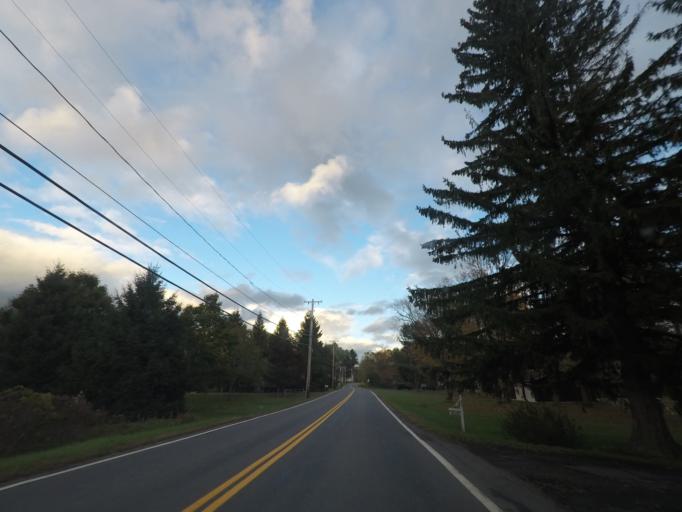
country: US
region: New York
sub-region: Rensselaer County
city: Nassau
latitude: 42.5571
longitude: -73.6263
